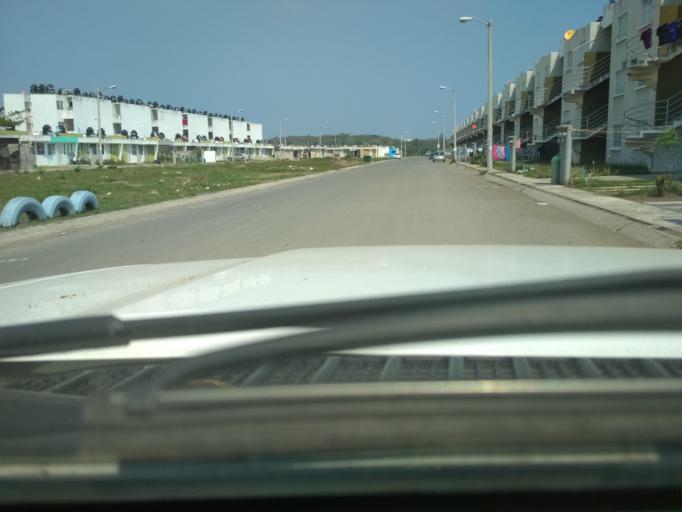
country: MX
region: Veracruz
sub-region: Veracruz
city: Lomas de Rio Medio Cuatro
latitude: 19.1864
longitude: -96.2069
